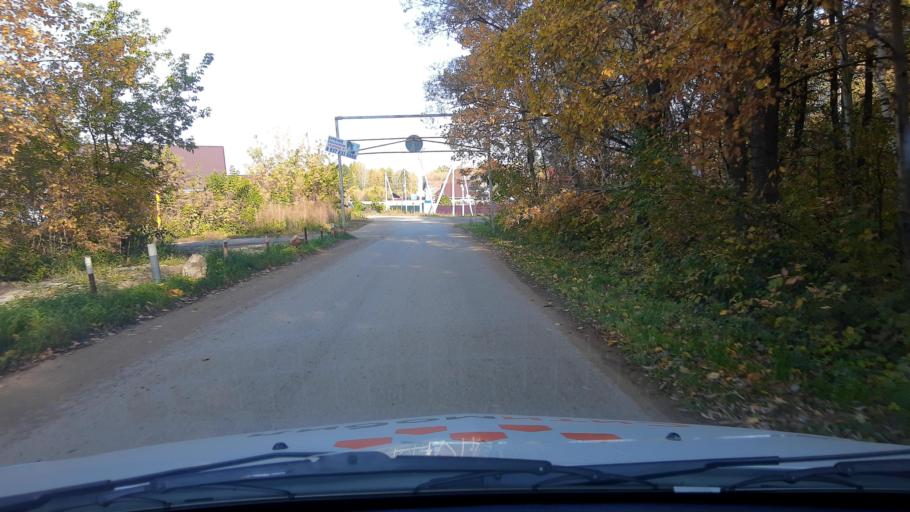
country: RU
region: Bashkortostan
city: Ufa
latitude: 54.6627
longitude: 56.0594
